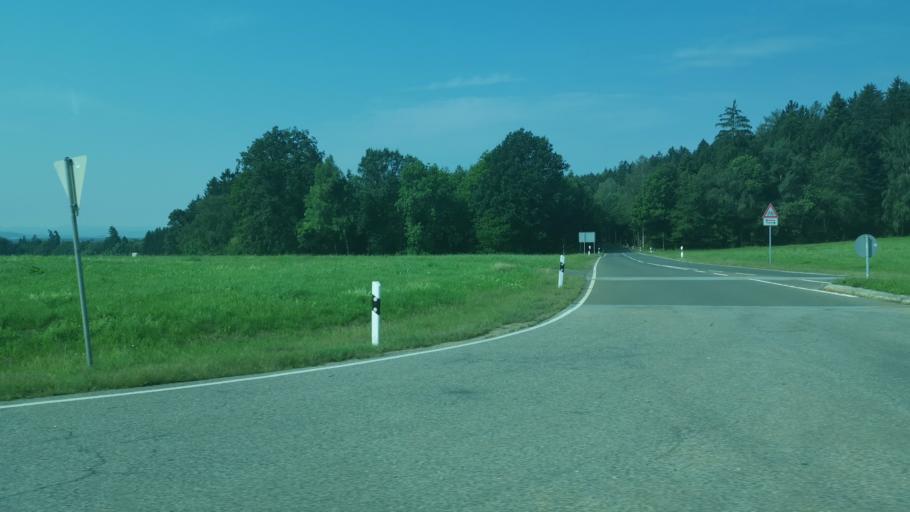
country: DE
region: Bavaria
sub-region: Upper Palatinate
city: Pemfling
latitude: 49.2726
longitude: 12.6305
